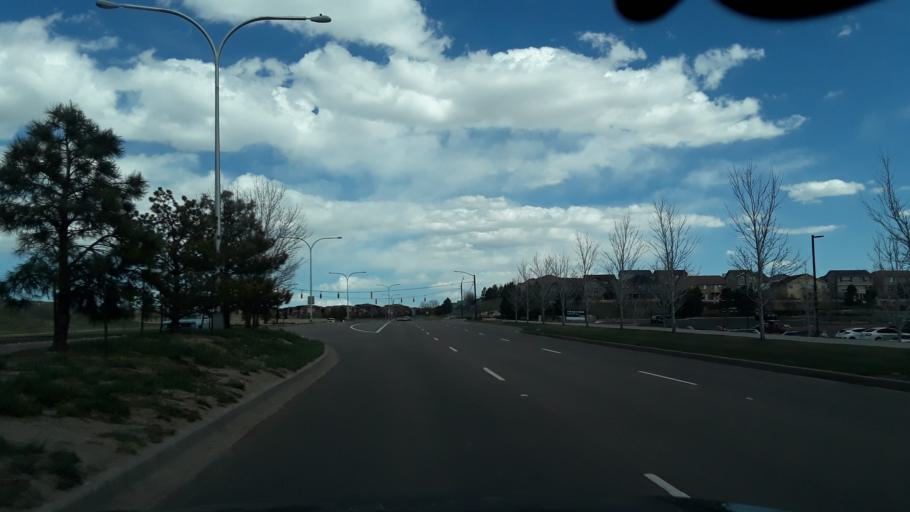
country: US
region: Colorado
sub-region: El Paso County
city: Black Forest
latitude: 38.9658
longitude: -104.7532
